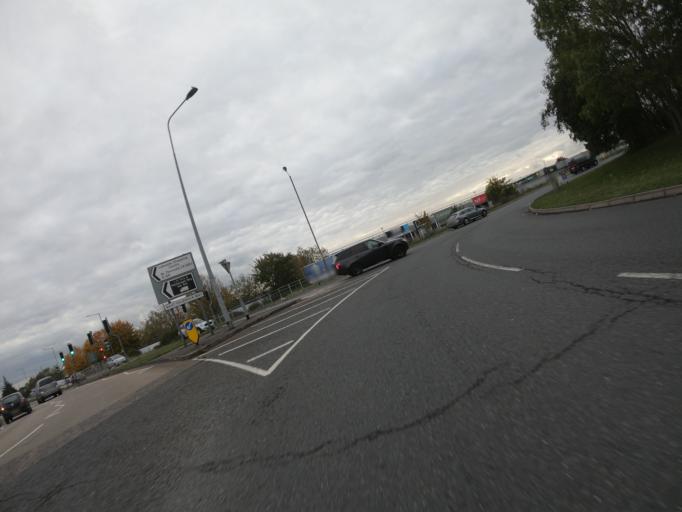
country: GB
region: England
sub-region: Kent
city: West Thurrock
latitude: 51.4855
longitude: 0.2745
